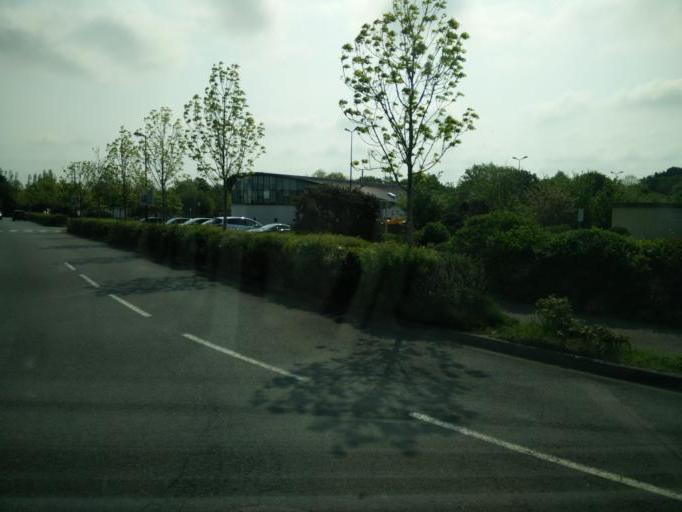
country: FR
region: Brittany
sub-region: Departement du Finistere
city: Moelan-sur-Mer
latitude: 47.8108
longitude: -3.6302
